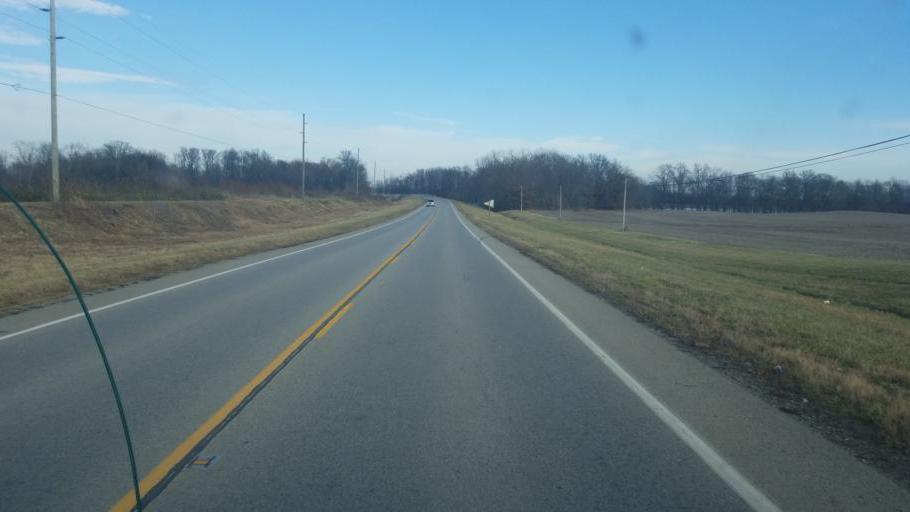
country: US
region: Illinois
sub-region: White County
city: Carmi
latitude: 38.1066
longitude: -88.1290
